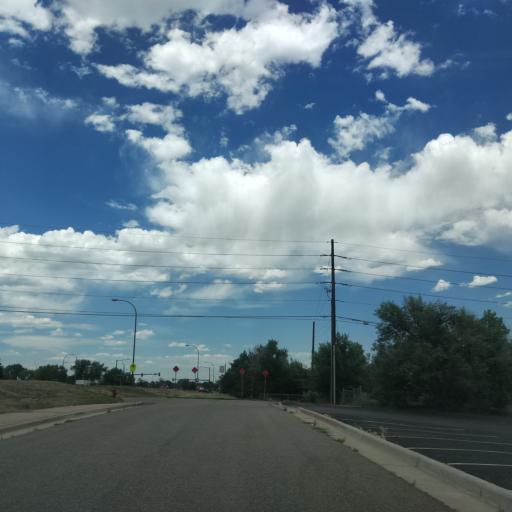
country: US
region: Colorado
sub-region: Jefferson County
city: Lakewood
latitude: 39.7089
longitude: -105.1093
